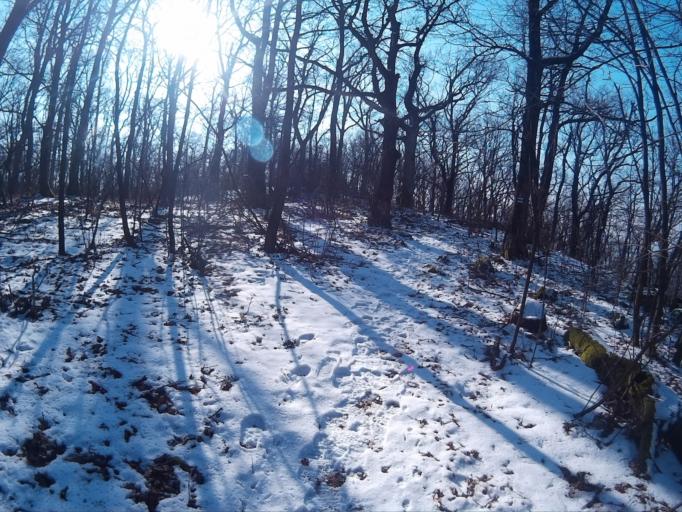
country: HU
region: Nograd
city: Paszto
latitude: 47.9631
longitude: 19.6448
